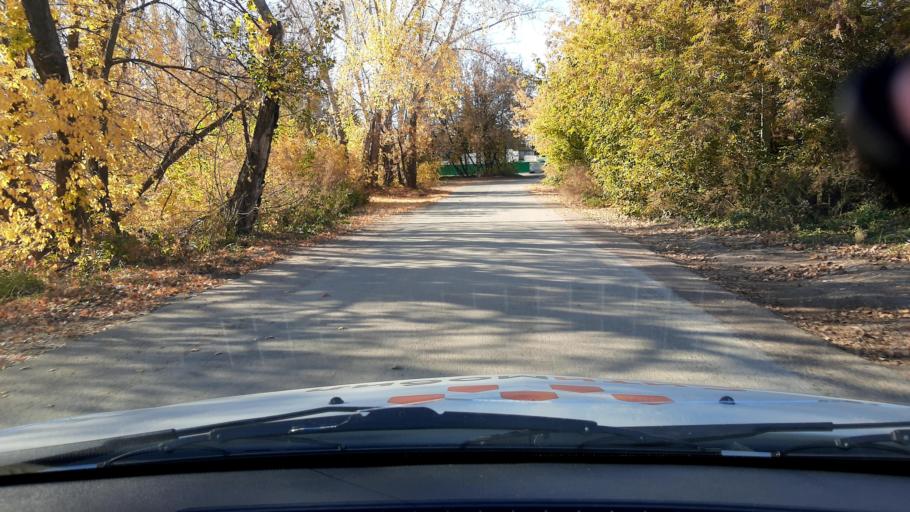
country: RU
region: Bashkortostan
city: Ufa
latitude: 54.7960
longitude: 56.0901
